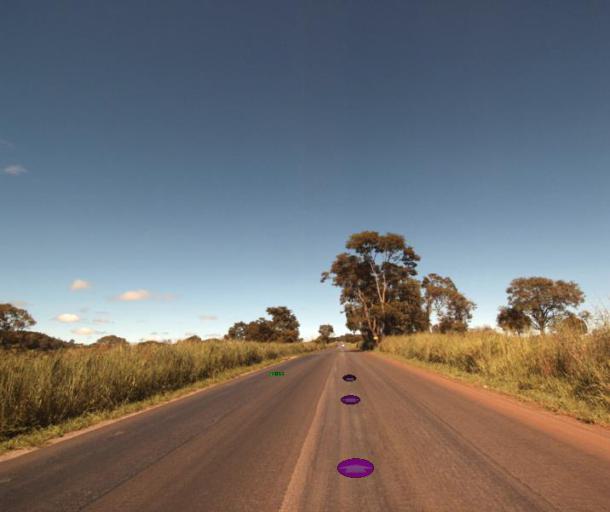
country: BR
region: Goias
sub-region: Itapaci
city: Itapaci
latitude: -15.1353
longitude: -49.5191
